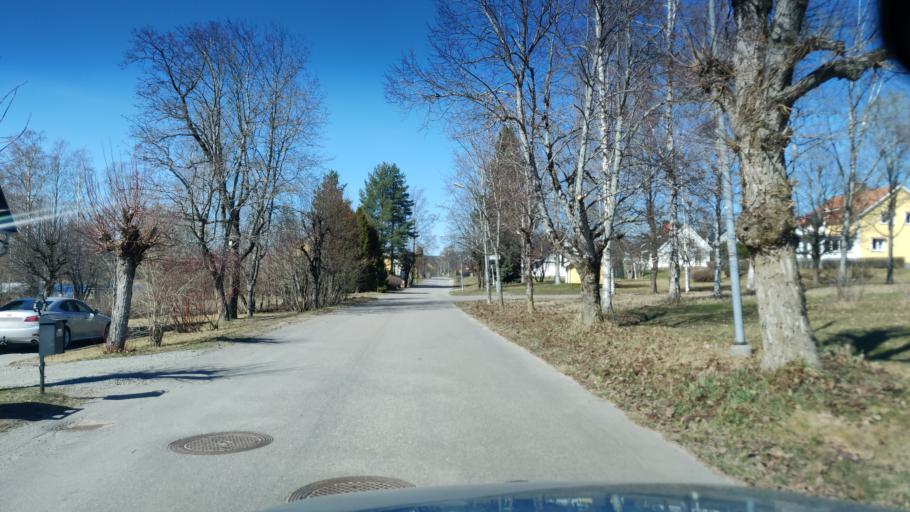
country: SE
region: Vaermland
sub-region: Hagfors Kommun
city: Hagfors
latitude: 60.0351
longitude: 13.6852
